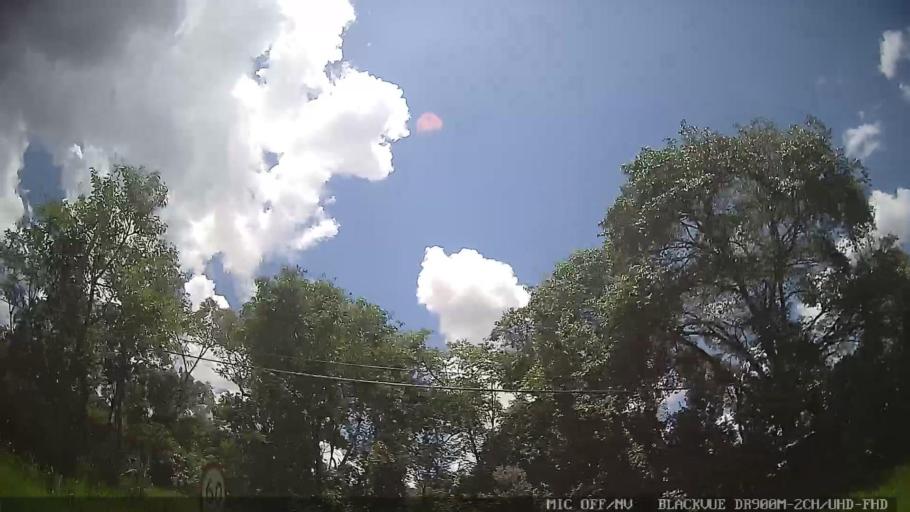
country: BR
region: Sao Paulo
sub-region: Amparo
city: Amparo
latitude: -22.6801
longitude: -46.7403
